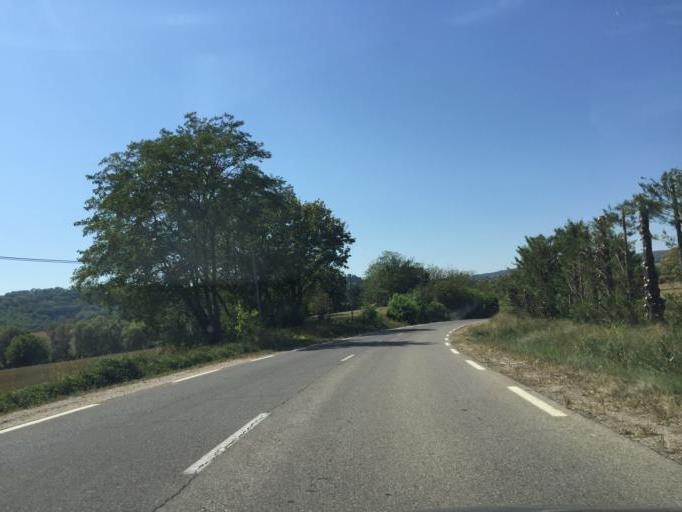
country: FR
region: Provence-Alpes-Cote d'Azur
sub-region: Departement des Alpes-de-Haute-Provence
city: Forcalquier
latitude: 43.9559
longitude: 5.8100
